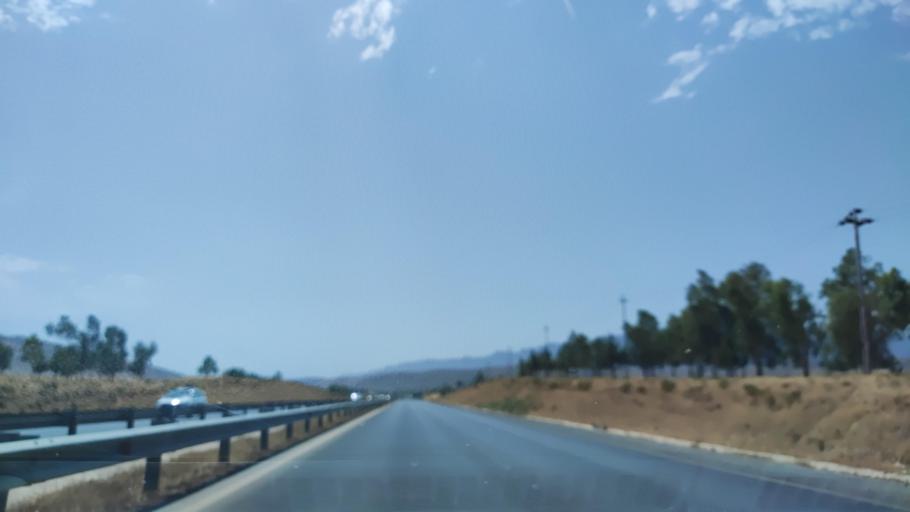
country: IQ
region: Arbil
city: Shaqlawah
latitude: 36.4677
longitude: 44.3825
